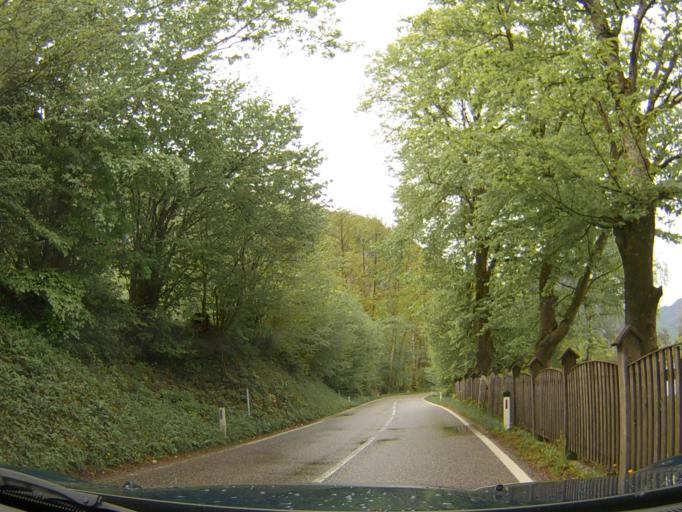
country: AT
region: Upper Austria
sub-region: Politischer Bezirk Vocklabruck
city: Innerschwand
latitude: 47.8027
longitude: 13.4477
